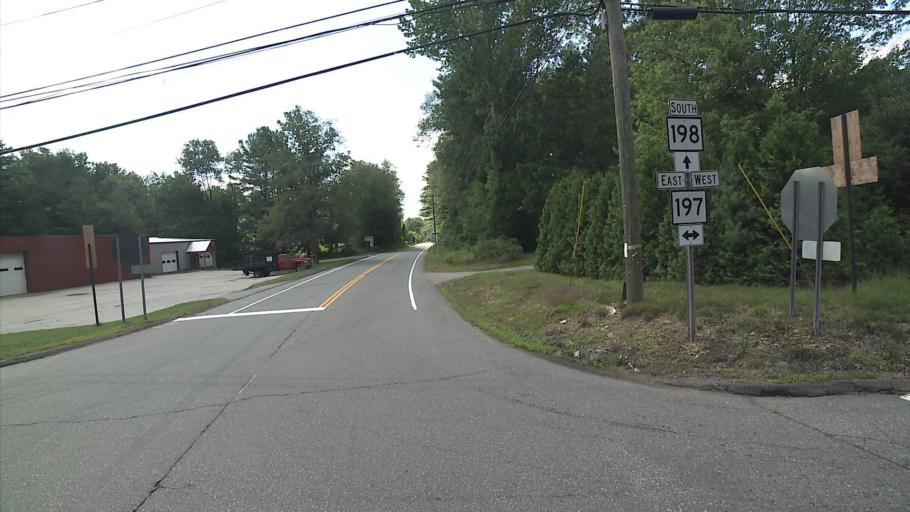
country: US
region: Massachusetts
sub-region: Worcester County
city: Southbridge
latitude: 41.9823
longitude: -72.0822
